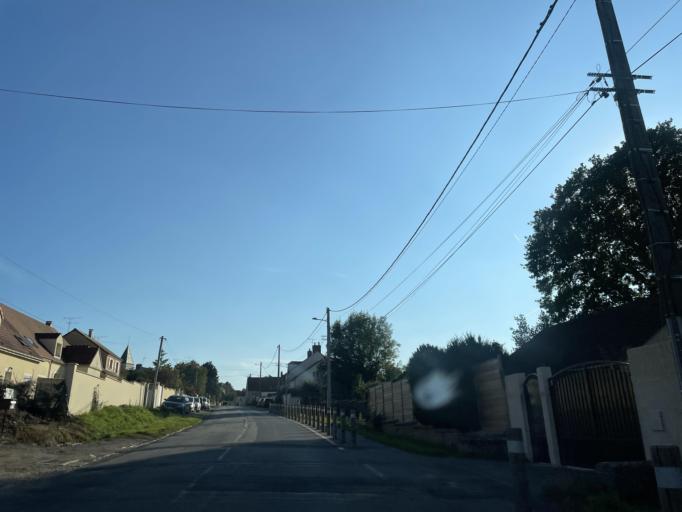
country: FR
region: Ile-de-France
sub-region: Departement de Seine-et-Marne
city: Voulangis
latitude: 48.8524
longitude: 2.8988
